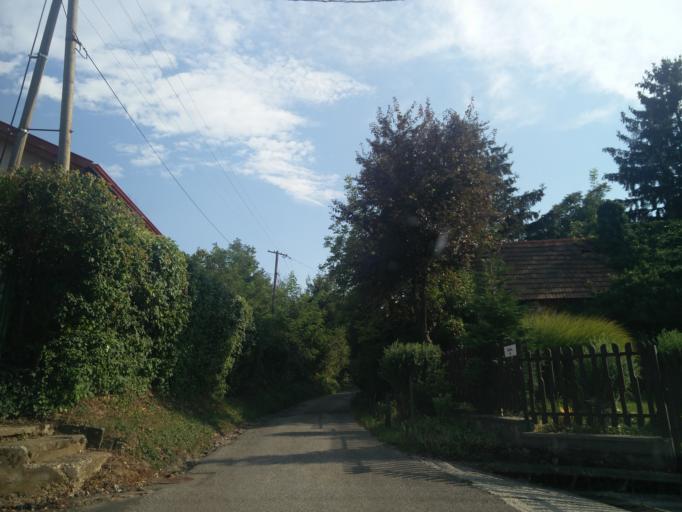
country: HU
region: Zala
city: Zalaegerszeg
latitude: 46.8384
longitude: 16.8101
